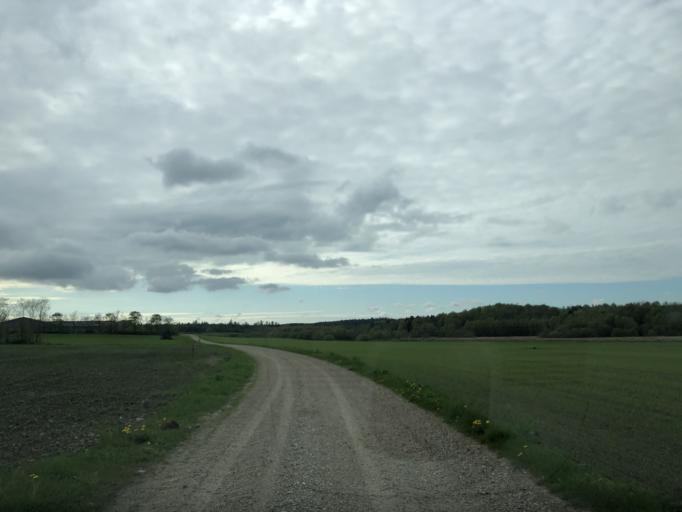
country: DK
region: Central Jutland
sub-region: Holstebro Kommune
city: Ulfborg
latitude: 56.1964
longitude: 8.4568
